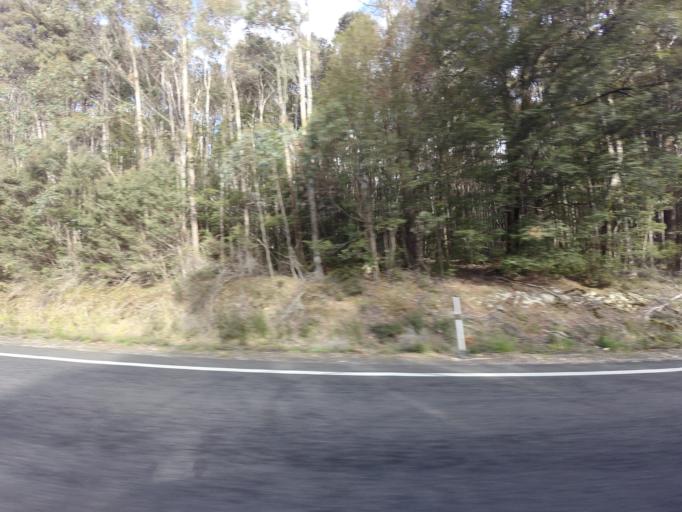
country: AU
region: Tasmania
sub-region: Meander Valley
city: Deloraine
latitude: -41.7067
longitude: 146.7176
